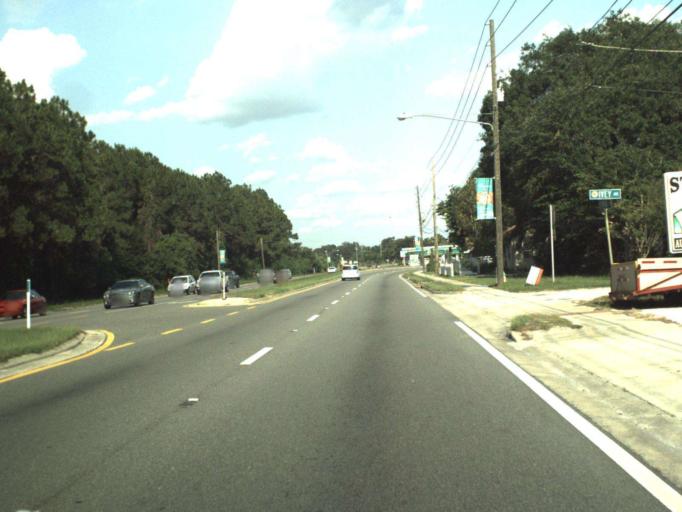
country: US
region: Florida
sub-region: Lake County
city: Groveland
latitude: 28.5633
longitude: -81.8630
